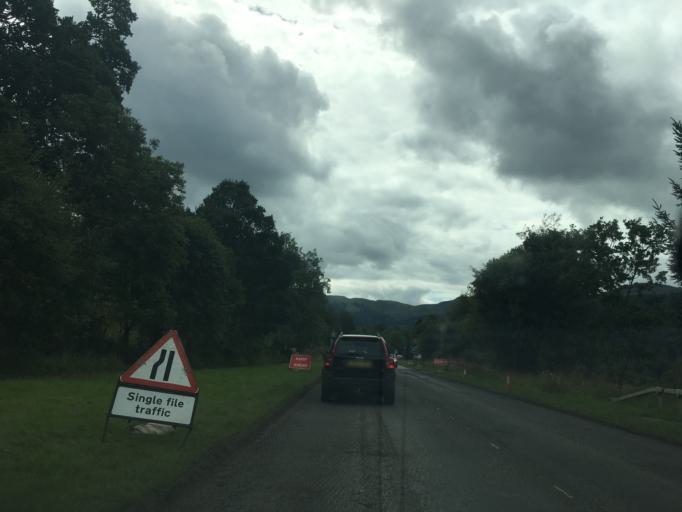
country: GB
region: Scotland
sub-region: Stirling
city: Callander
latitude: 56.3306
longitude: -4.3248
